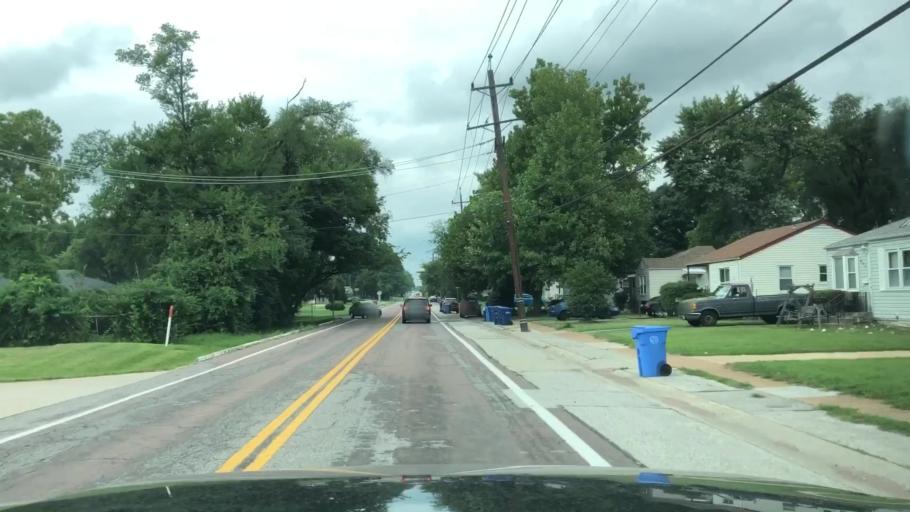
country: US
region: Missouri
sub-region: Saint Louis County
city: Florissant
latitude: 38.8016
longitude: -90.3466
